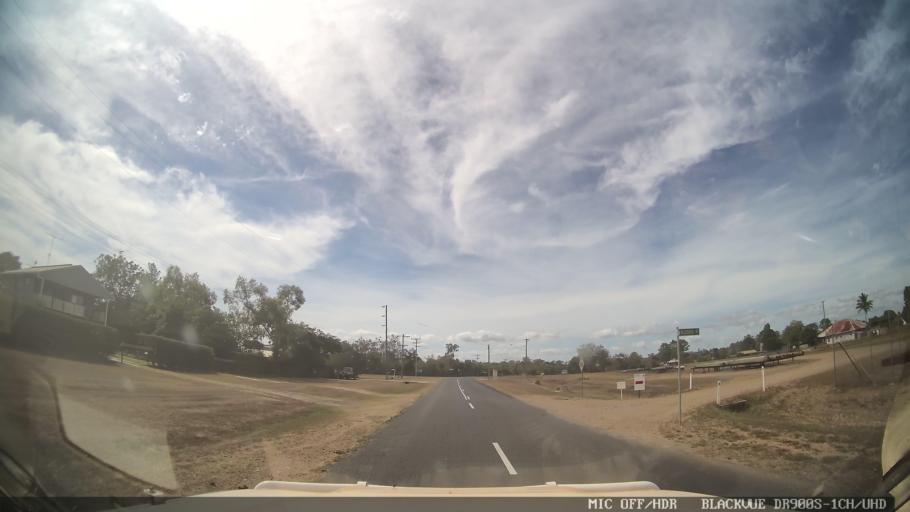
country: AU
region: Queensland
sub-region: Tablelands
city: Mareeba
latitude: -16.9200
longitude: 145.4194
